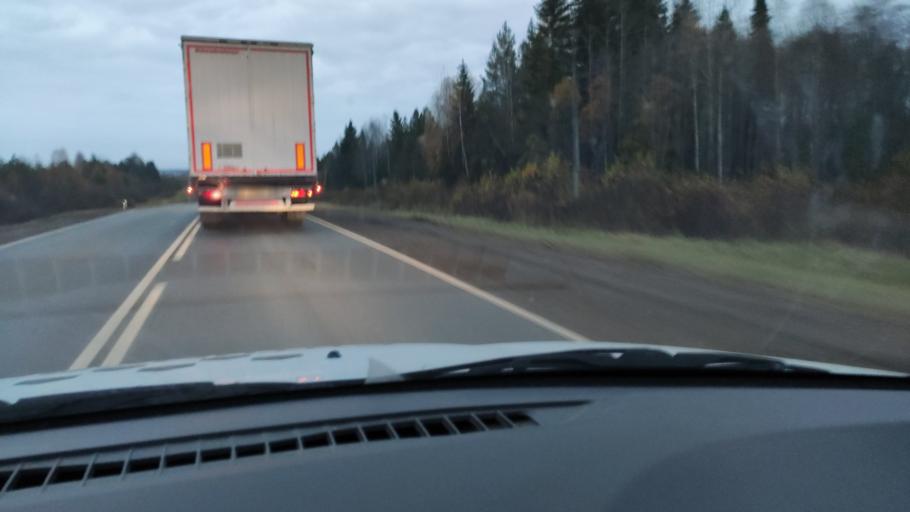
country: RU
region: Kirov
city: Kostino
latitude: 58.8551
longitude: 53.2000
